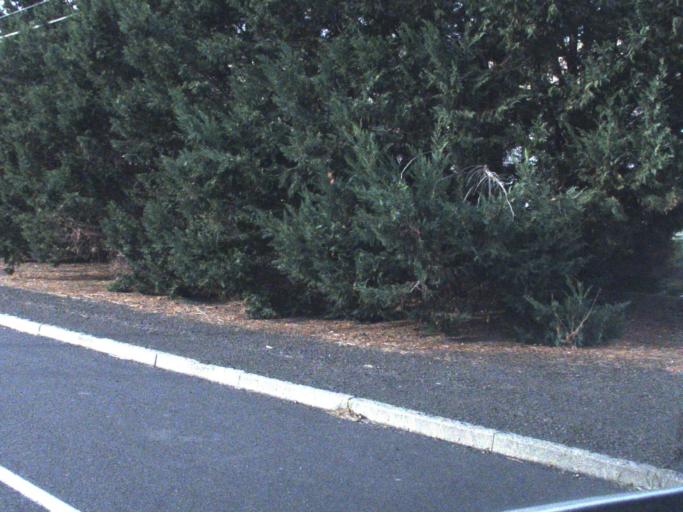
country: US
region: Washington
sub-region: Garfield County
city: Pomeroy
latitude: 46.4748
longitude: -117.5764
